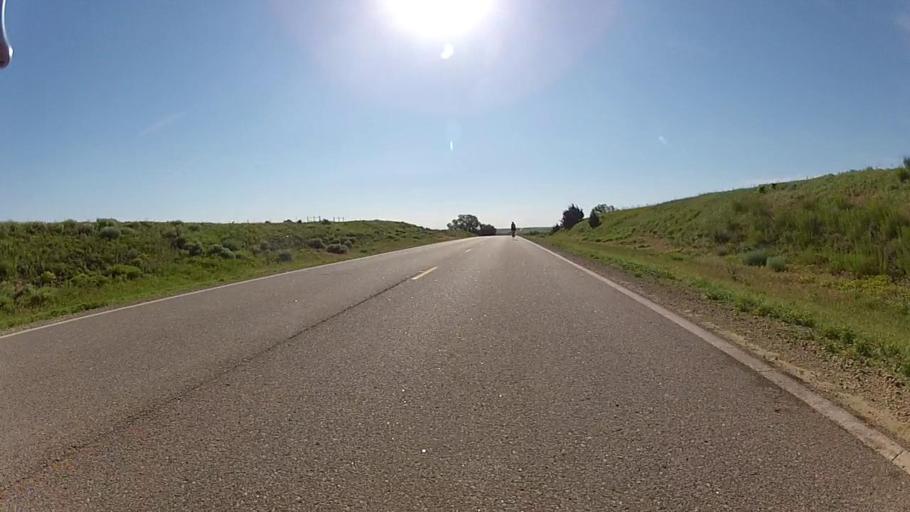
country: US
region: Kansas
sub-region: Barber County
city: Medicine Lodge
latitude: 37.2816
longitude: -98.8890
